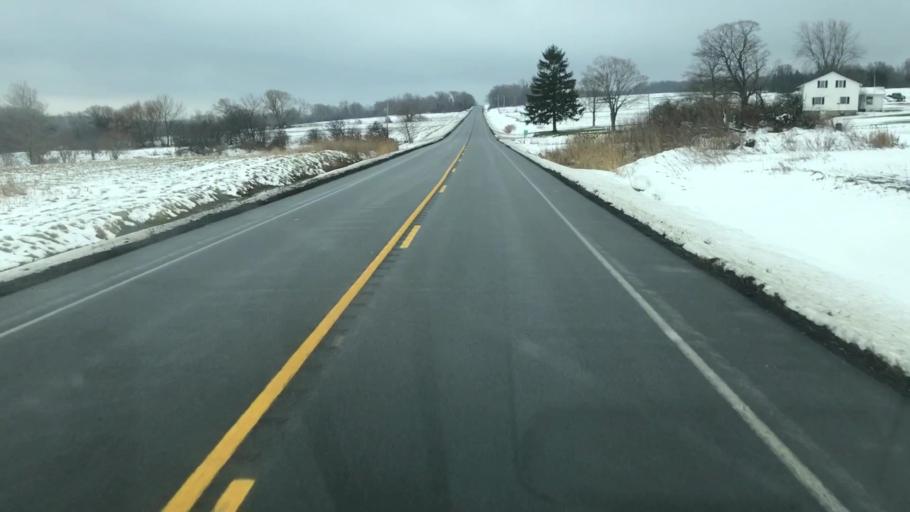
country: US
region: New York
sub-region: Cayuga County
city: Moravia
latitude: 42.7841
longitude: -76.3432
